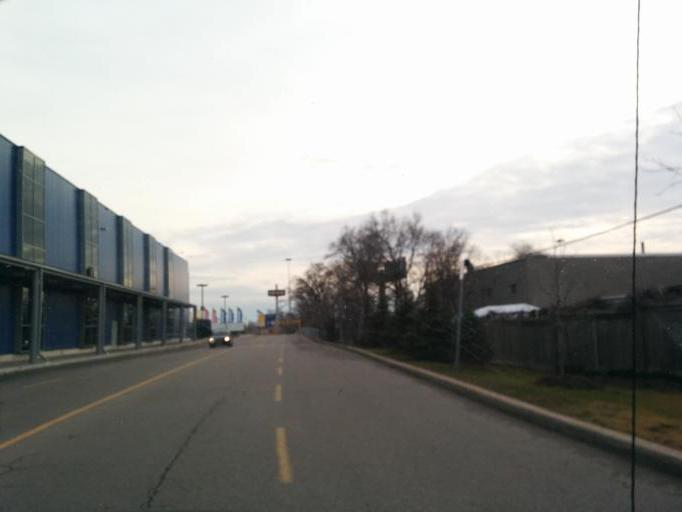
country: CA
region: Ontario
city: Etobicoke
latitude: 43.6185
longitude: -79.5361
